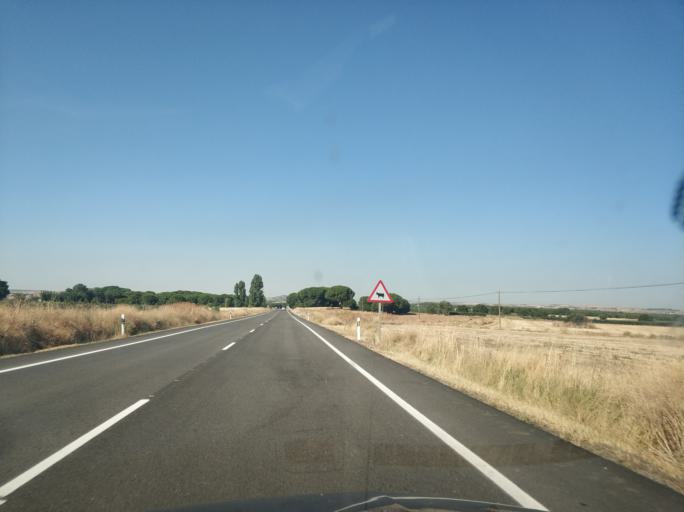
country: ES
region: Castille and Leon
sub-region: Provincia de Burgos
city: Fuentelisendo
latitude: 41.6160
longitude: -3.9179
